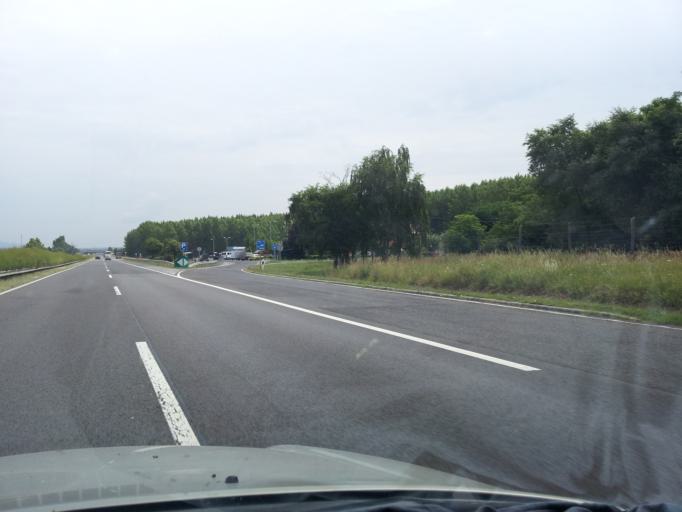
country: HU
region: Heves
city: Hort
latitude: 47.6877
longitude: 19.7395
